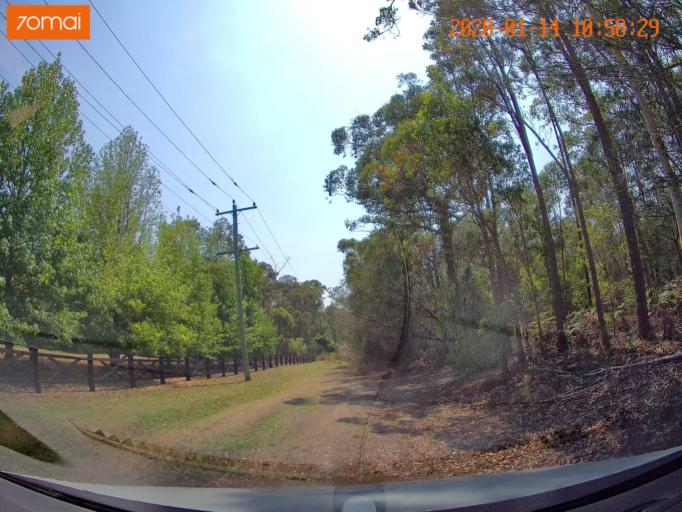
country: AU
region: New South Wales
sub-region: Lake Macquarie Shire
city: Dora Creek
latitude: -33.0993
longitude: 151.4915
